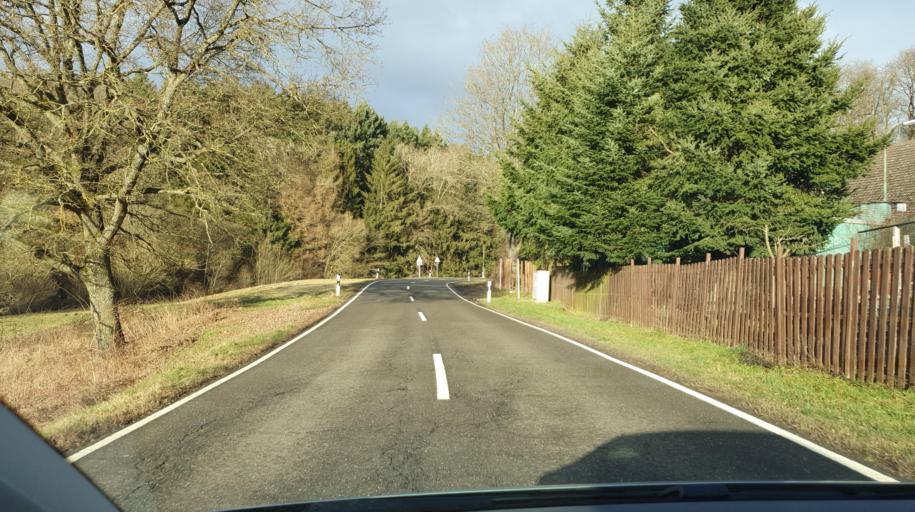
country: DE
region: Rheinland-Pfalz
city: Blaubach
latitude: 49.5617
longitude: 7.4008
